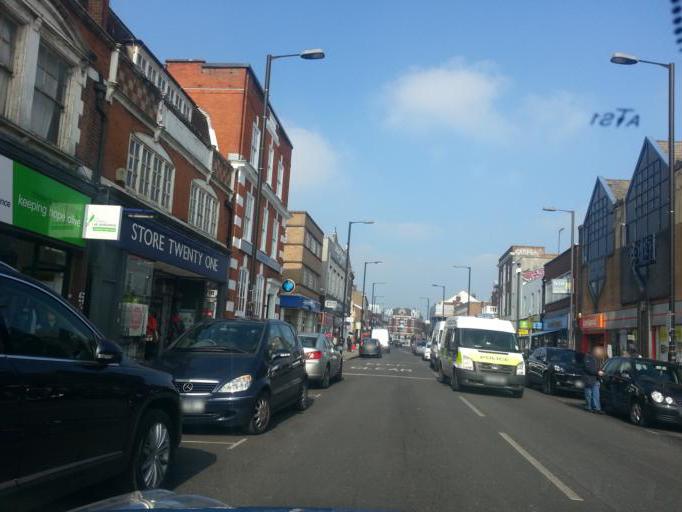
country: GB
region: England
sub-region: Greater London
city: Barnet
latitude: 51.6545
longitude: -0.2016
